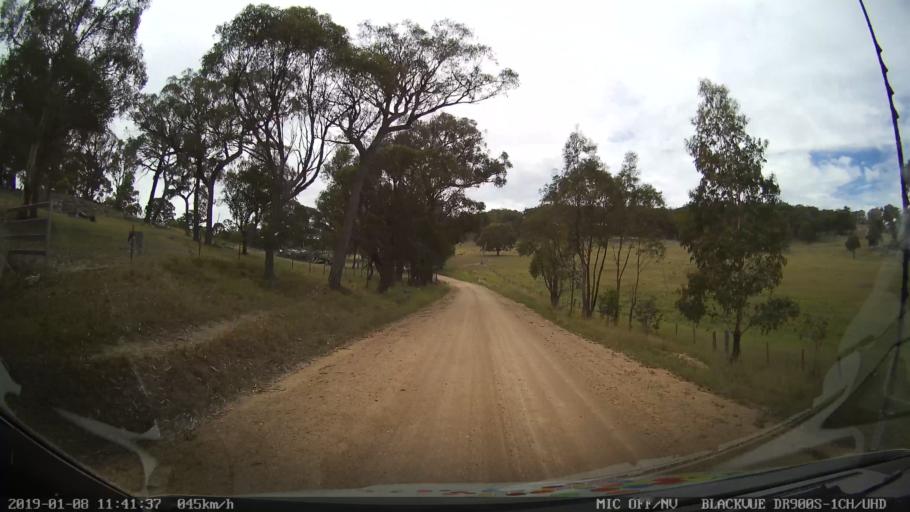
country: AU
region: New South Wales
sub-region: Armidale Dumaresq
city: Armidale
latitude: -30.3772
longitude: 151.5694
